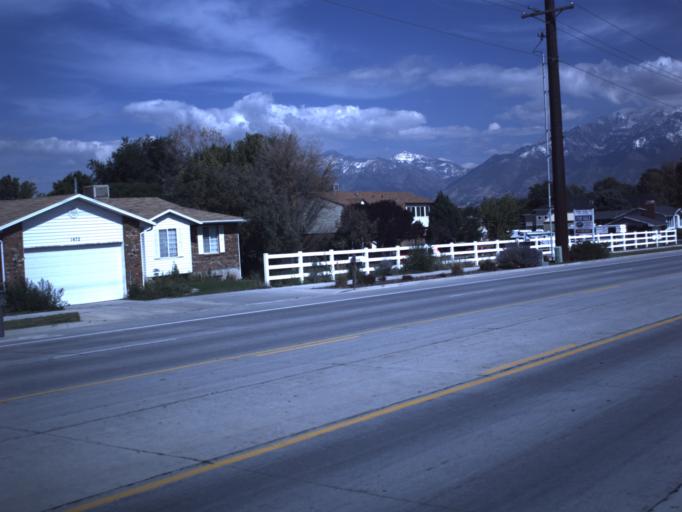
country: US
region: Utah
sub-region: Salt Lake County
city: South Jordan
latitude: 40.5441
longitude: -111.9337
